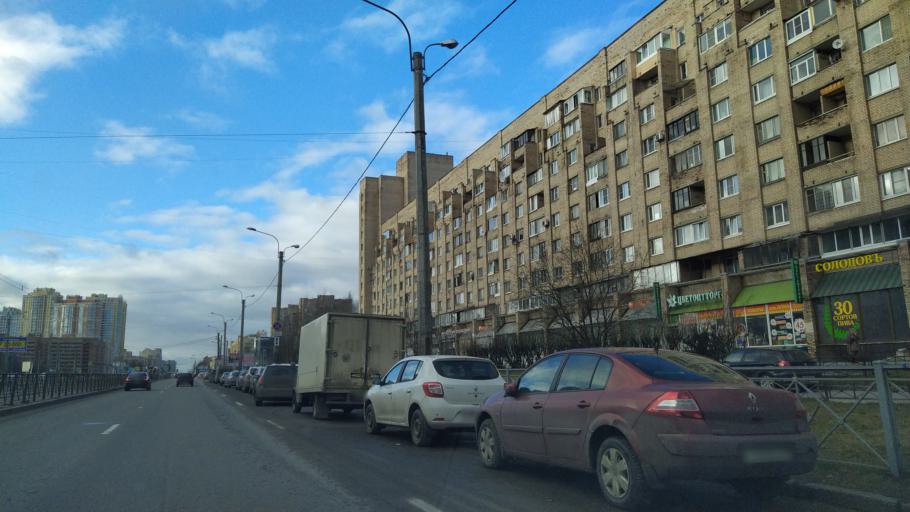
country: RU
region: St.-Petersburg
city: Grazhdanka
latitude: 60.0439
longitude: 30.3795
